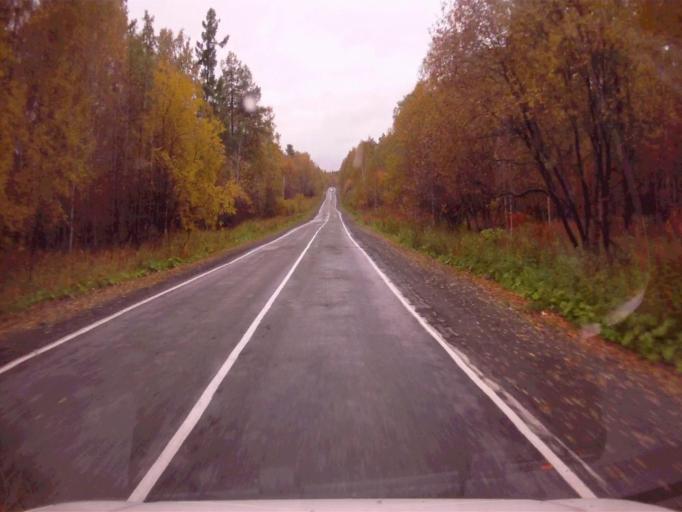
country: RU
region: Chelyabinsk
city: Nizhniy Ufaley
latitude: 56.0512
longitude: 59.9493
